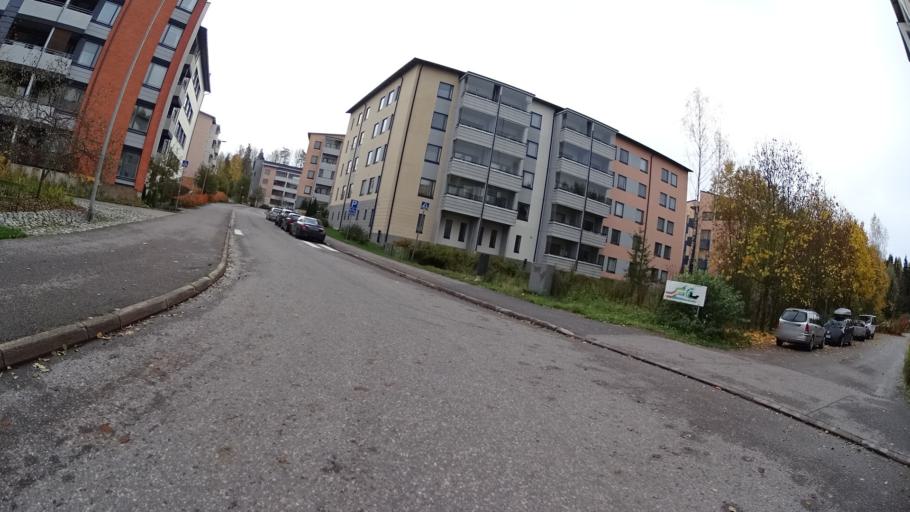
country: FI
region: Uusimaa
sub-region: Helsinki
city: Kauniainen
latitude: 60.2052
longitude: 24.7044
